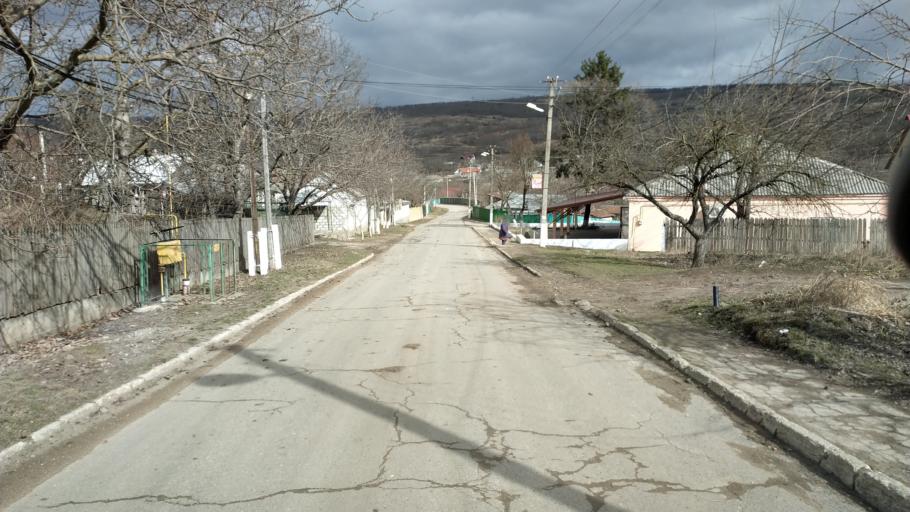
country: MD
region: Stinga Nistrului
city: Bucovat
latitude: 47.2288
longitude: 28.4419
